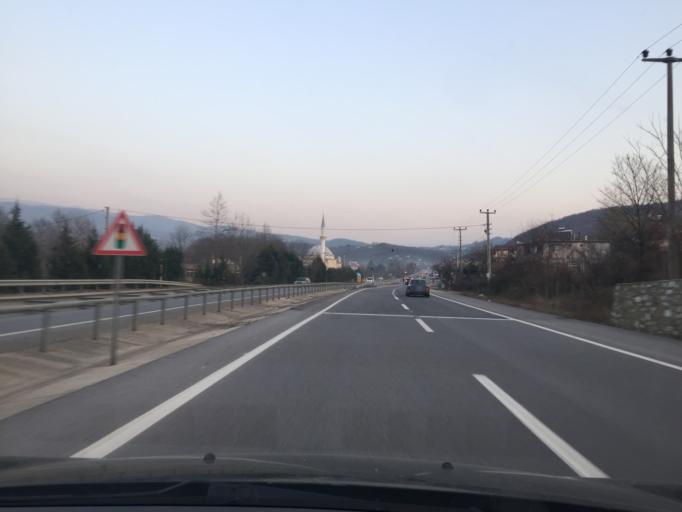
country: TR
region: Sakarya
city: Akyazi
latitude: 40.6255
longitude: 30.6493
